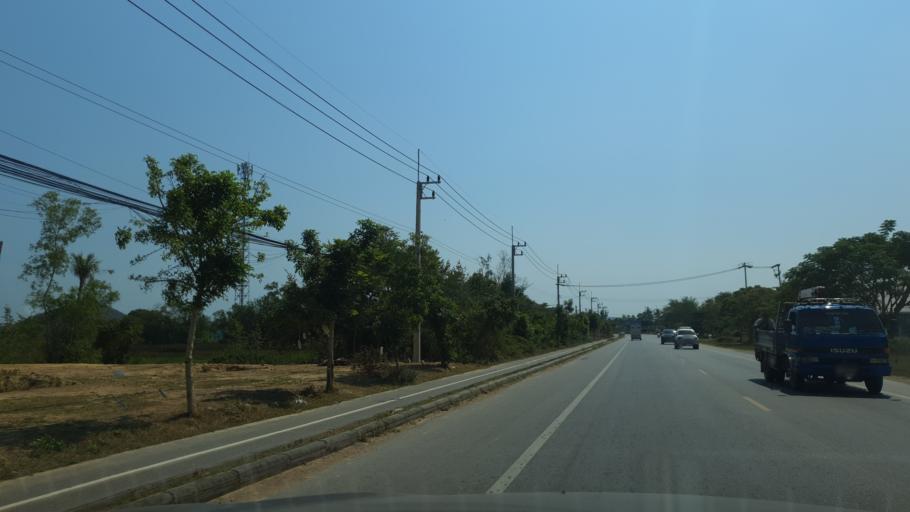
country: TH
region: Prachuap Khiri Khan
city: Pran Buri
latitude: 12.3443
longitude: 99.9424
